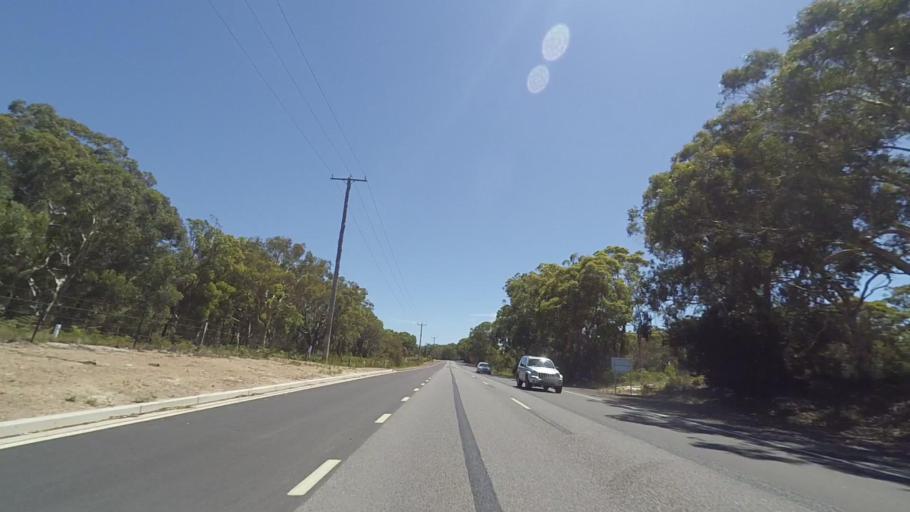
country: AU
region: New South Wales
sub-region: Port Stephens Shire
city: Medowie
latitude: -32.7834
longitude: 151.8578
